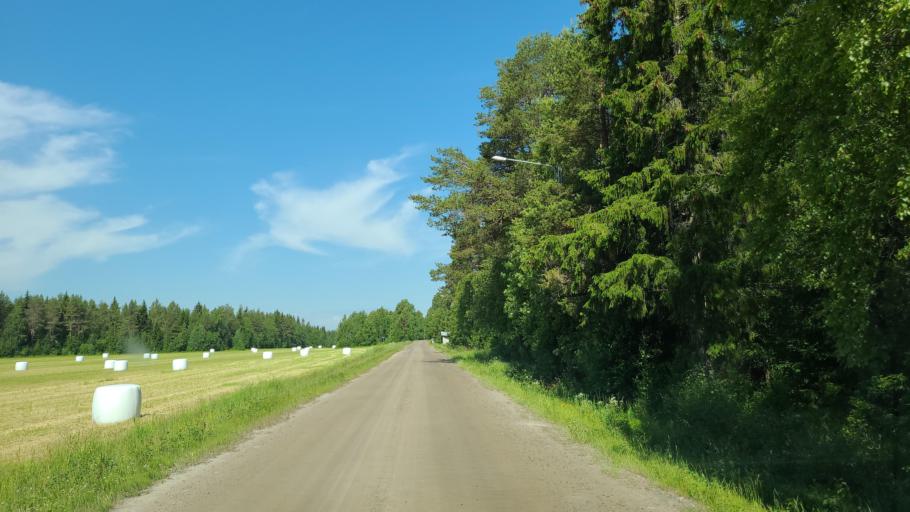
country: SE
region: Vaesterbotten
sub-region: Robertsfors Kommun
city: Robertsfors
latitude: 64.0827
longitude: 20.8464
